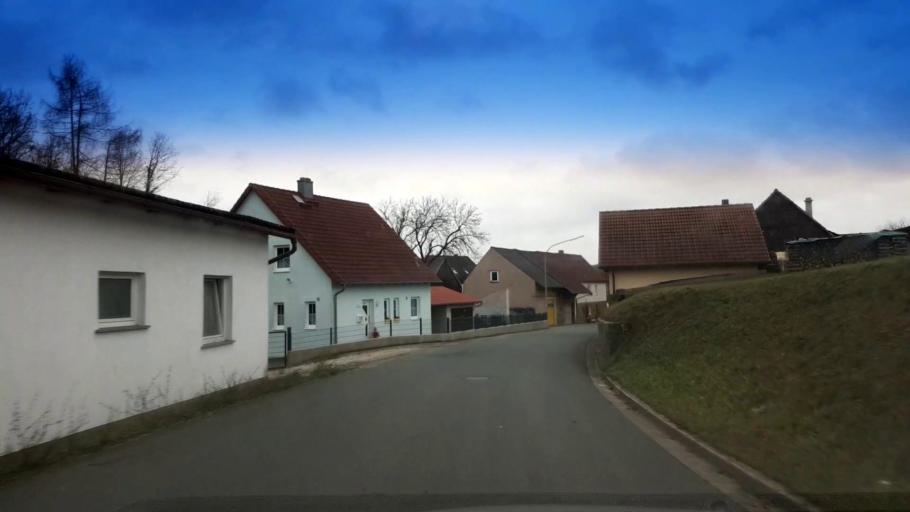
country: DE
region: Bavaria
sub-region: Upper Franconia
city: Rattelsdorf
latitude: 50.0499
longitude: 10.8876
